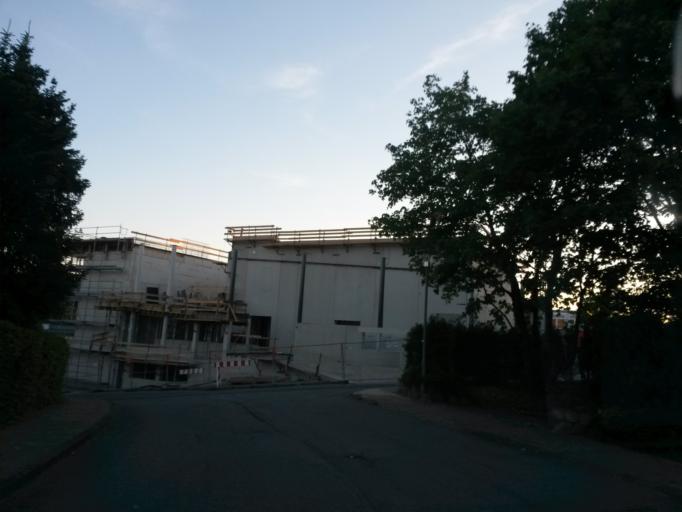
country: DE
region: North Rhine-Westphalia
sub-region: Regierungsbezirk Arnsberg
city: Herscheid
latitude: 51.1825
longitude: 7.7421
